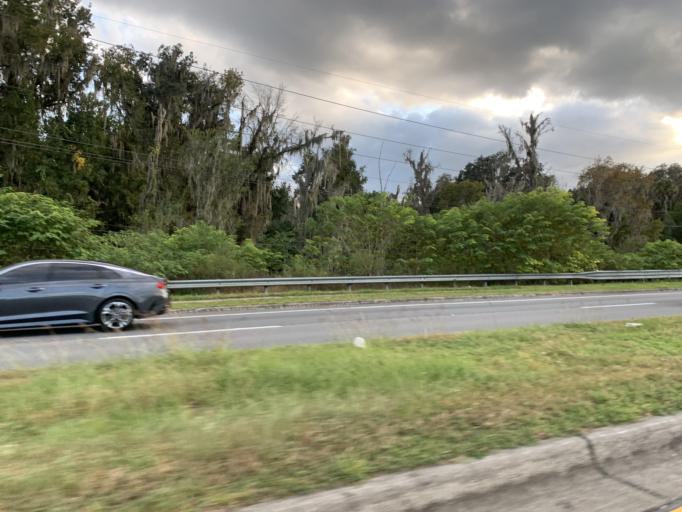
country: US
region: Florida
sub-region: Marion County
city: Ocala
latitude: 29.1562
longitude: -82.1397
